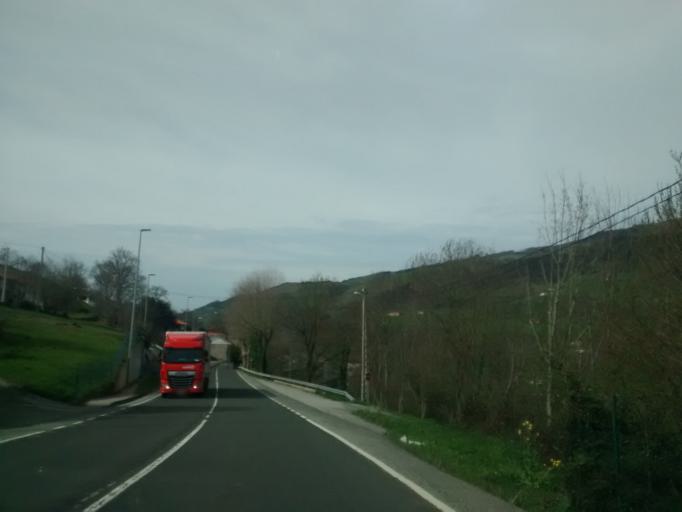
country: ES
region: Cantabria
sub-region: Provincia de Cantabria
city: Santiurde de Toranzo
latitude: 43.1875
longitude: -3.9124
